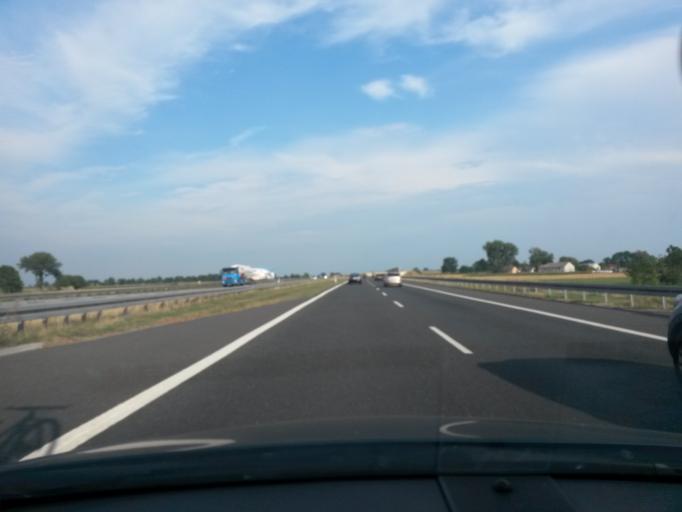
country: PL
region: Lodz Voivodeship
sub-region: Powiat poddebicki
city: Dalikow
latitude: 51.9648
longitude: 19.1127
